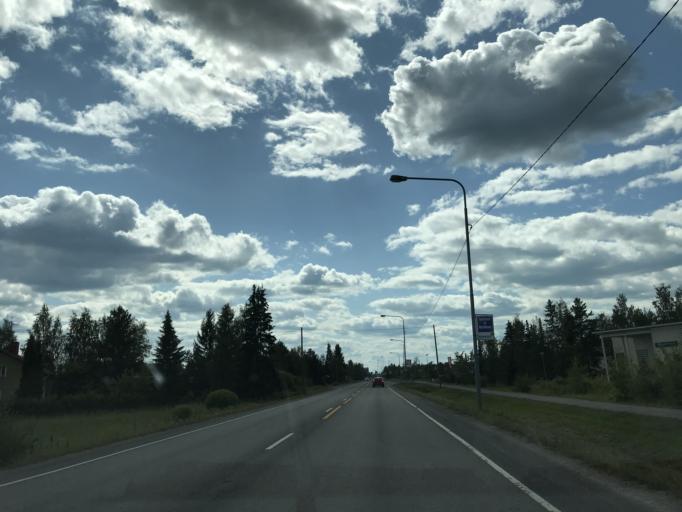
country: FI
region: Uusimaa
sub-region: Helsinki
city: Maentsaelae
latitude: 60.6463
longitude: 25.3318
